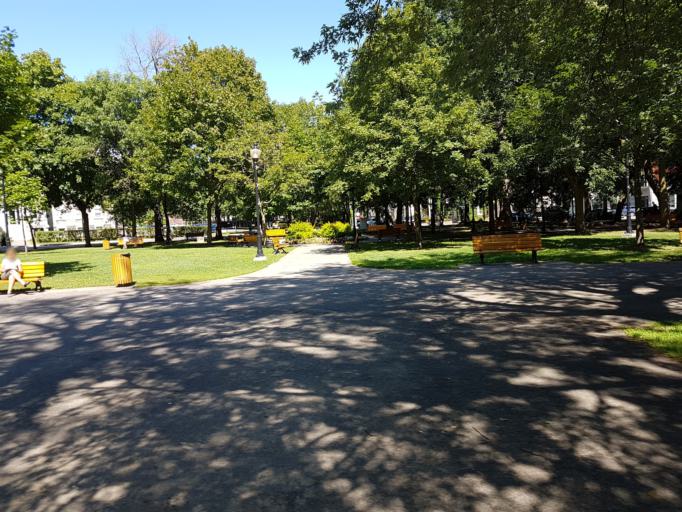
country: CA
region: Quebec
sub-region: Mauricie
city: Trois-Rivieres
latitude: 46.3435
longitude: -72.5428
